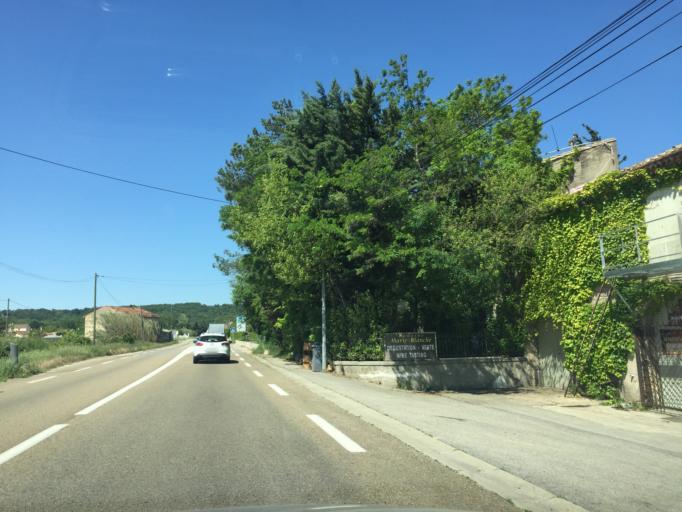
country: FR
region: Languedoc-Roussillon
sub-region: Departement du Gard
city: Saze
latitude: 43.9479
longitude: 4.6907
